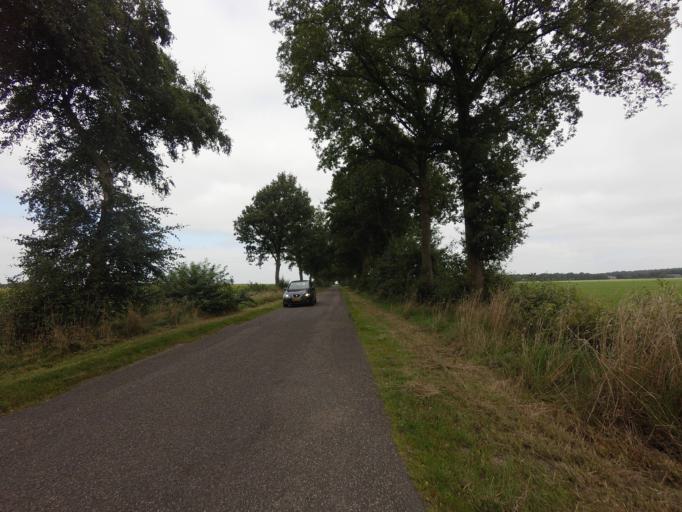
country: NL
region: Drenthe
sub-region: Gemeente Westerveld
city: Dwingeloo
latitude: 52.9701
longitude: 6.3583
